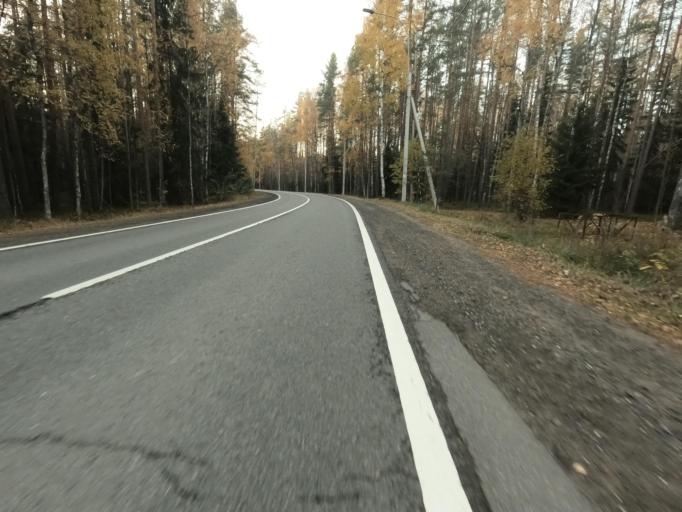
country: RU
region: St.-Petersburg
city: Repino
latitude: 60.1903
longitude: 29.8620
